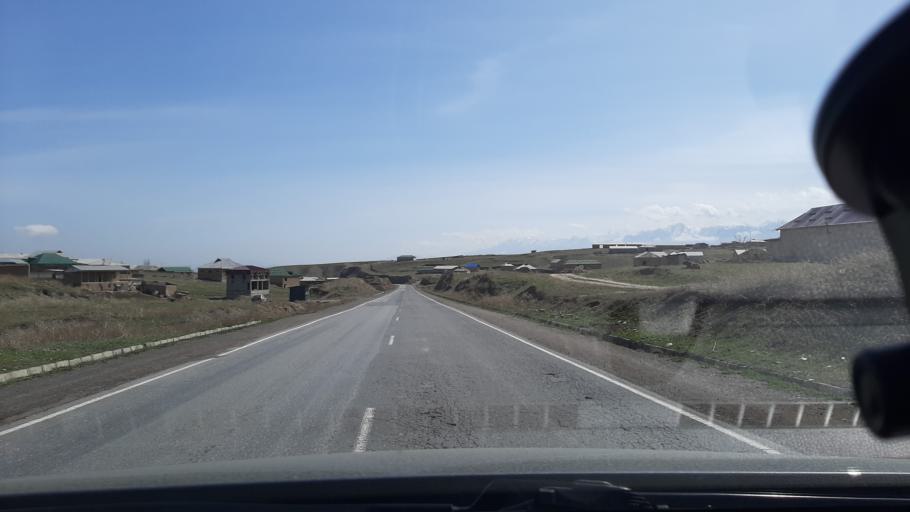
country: TJ
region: Viloyati Sughd
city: Shahriston
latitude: 39.7625
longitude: 68.8068
